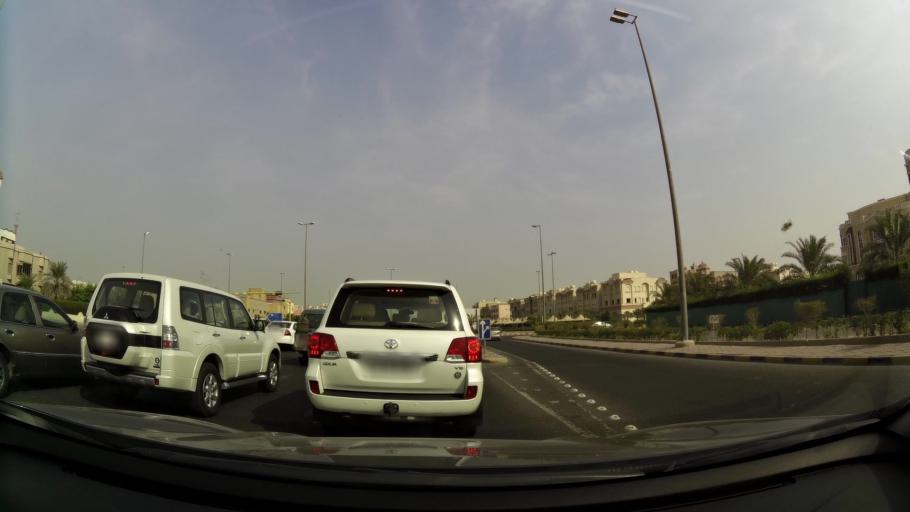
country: KW
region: Al Asimah
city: Ar Rabiyah
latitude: 29.2800
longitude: 47.9372
